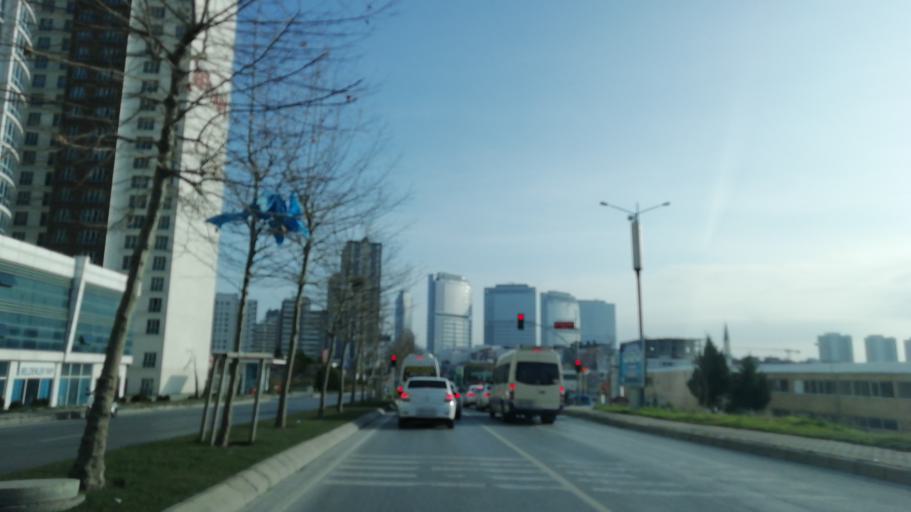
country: TR
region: Istanbul
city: Esenyurt
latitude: 41.0705
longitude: 28.6596
